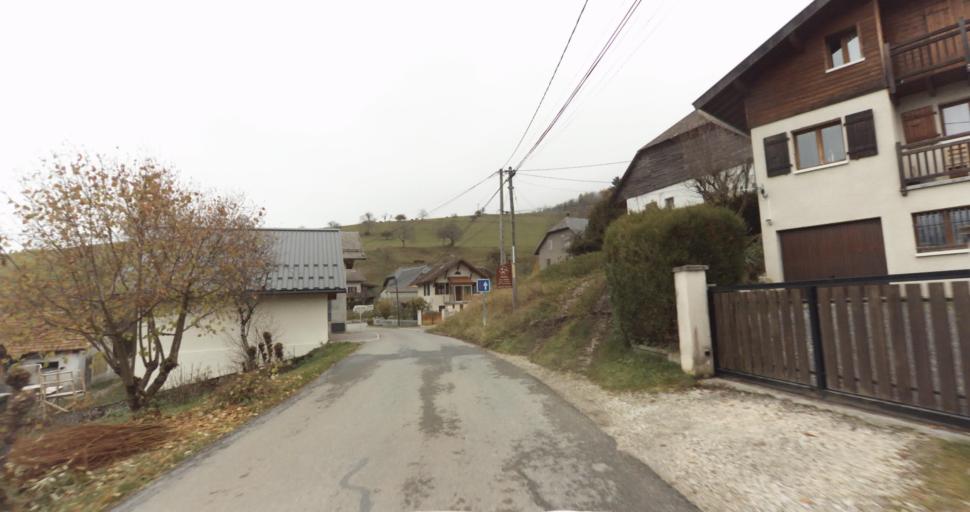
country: FR
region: Rhone-Alpes
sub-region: Departement de la Haute-Savoie
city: Saint-Jorioz
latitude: 45.7991
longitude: 6.1574
